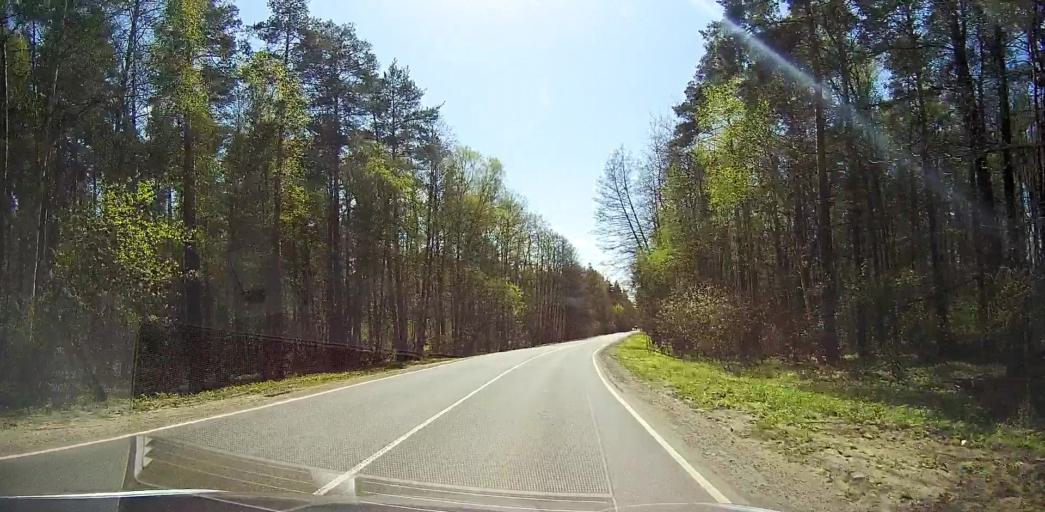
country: RU
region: Moskovskaya
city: Beloozerskiy
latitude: 55.4867
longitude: 38.4279
